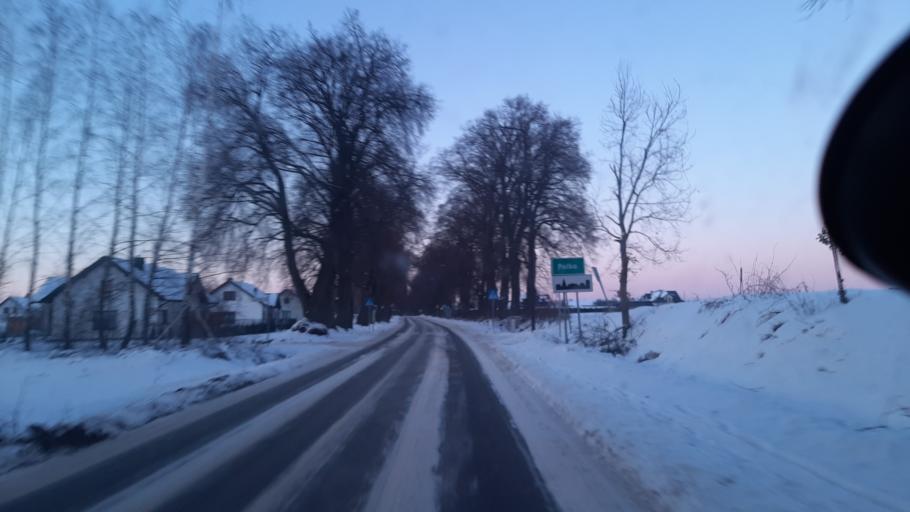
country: PL
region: Lublin Voivodeship
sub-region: Powiat lubelski
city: Lublin
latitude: 51.3213
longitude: 22.5611
